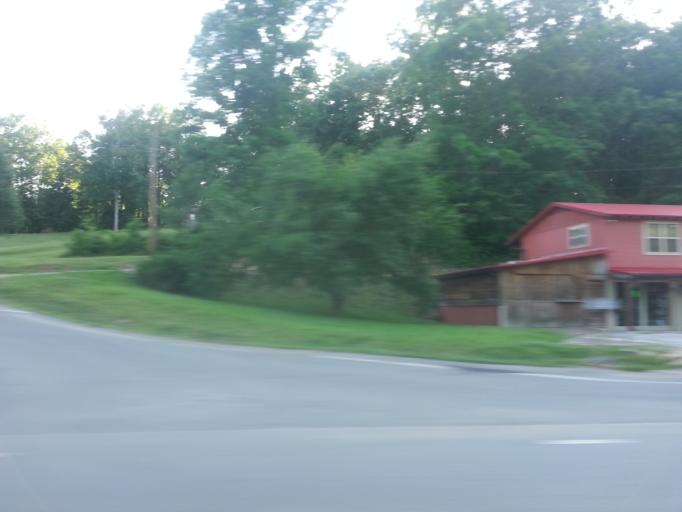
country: US
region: North Carolina
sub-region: Cherokee County
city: Murphy
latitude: 35.0095
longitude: -84.0847
